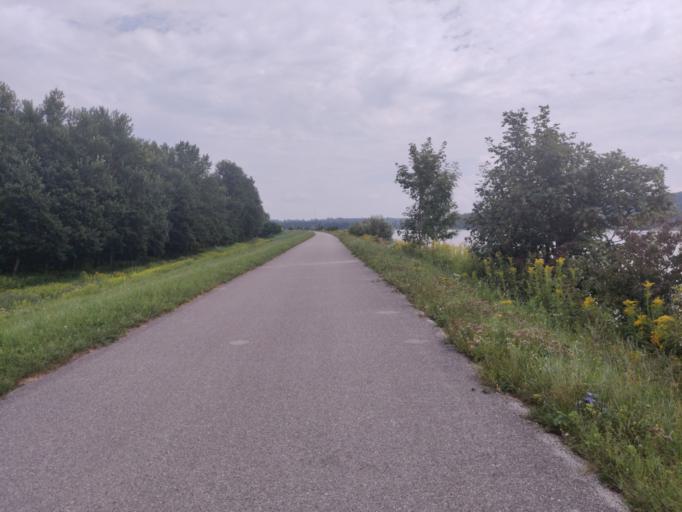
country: AT
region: Lower Austria
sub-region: Politischer Bezirk Amstetten
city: Strengberg
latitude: 48.1698
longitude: 14.6588
